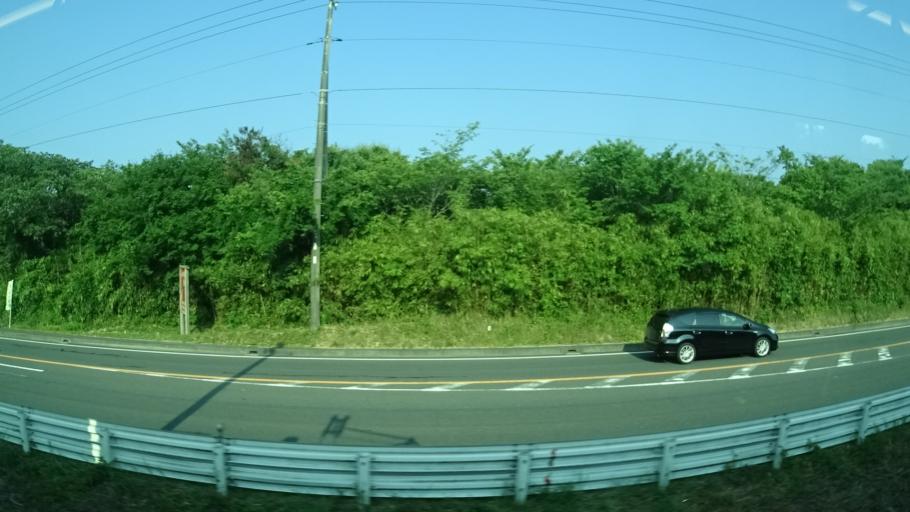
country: JP
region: Ibaraki
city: Kitaibaraki
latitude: 36.7699
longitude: 140.7387
